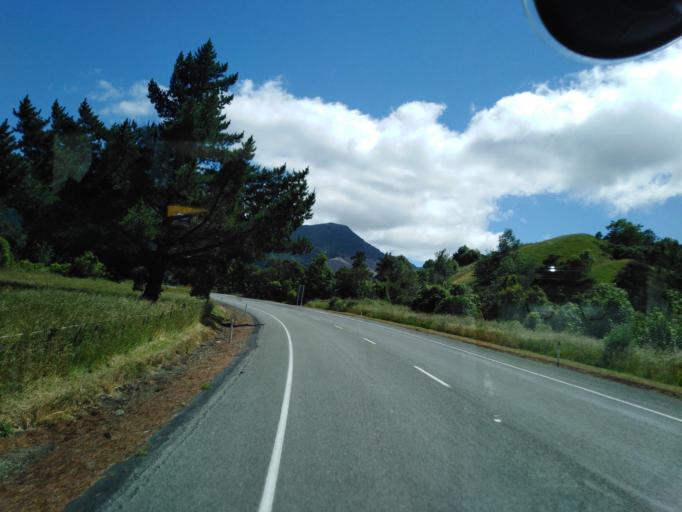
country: NZ
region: Nelson
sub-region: Nelson City
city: Nelson
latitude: -41.2203
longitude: 173.3980
